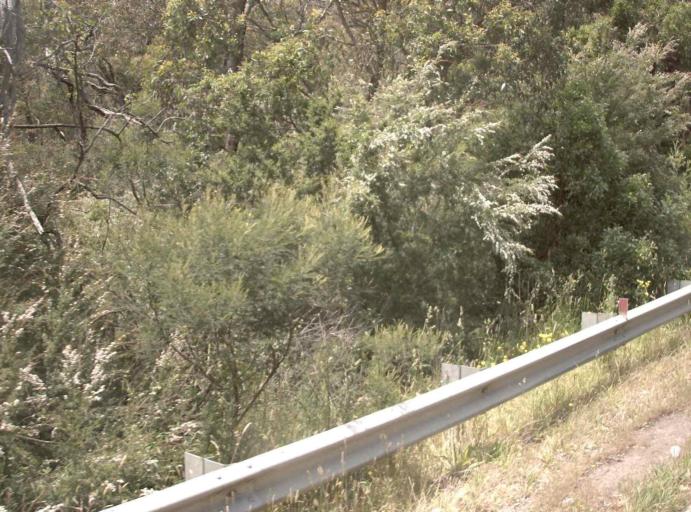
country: AU
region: Victoria
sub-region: Latrobe
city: Traralgon
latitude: -38.3013
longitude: 146.7064
